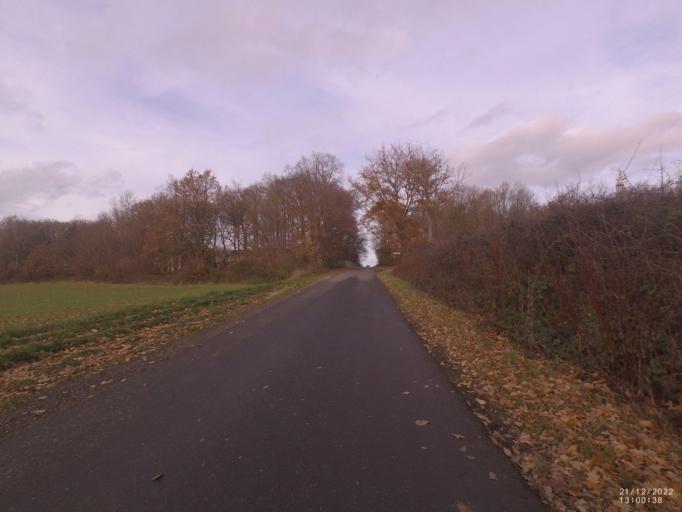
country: DE
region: Rheinland-Pfalz
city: Waldorf
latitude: 50.4921
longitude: 7.2322
